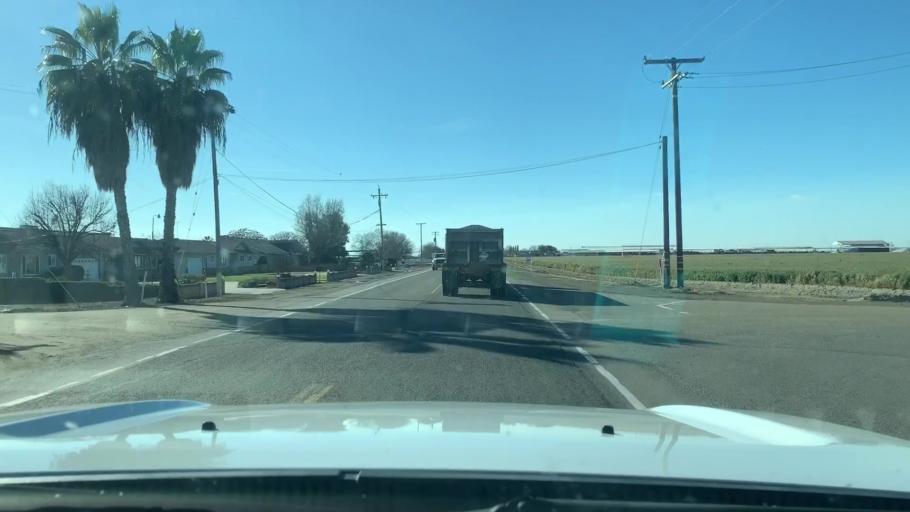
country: US
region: California
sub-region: Kings County
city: Corcoran
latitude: 36.2111
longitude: -119.5292
